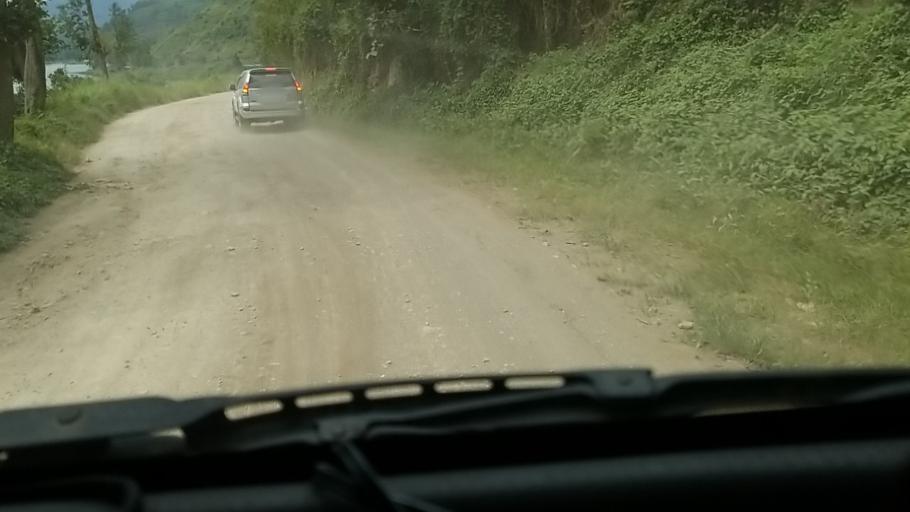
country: CD
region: Nord Kivu
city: Sake
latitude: -1.5902
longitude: 29.0433
